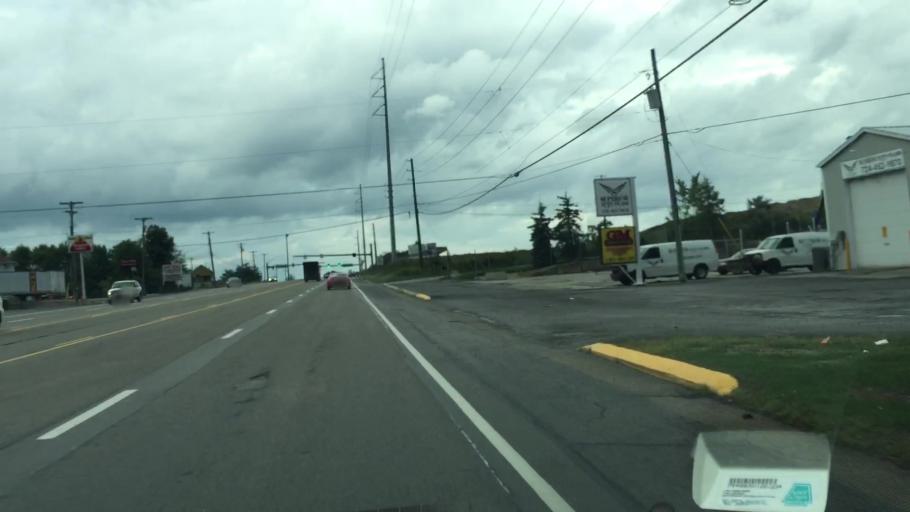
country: US
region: Pennsylvania
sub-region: Butler County
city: Zelienople
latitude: 40.7506
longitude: -80.1157
